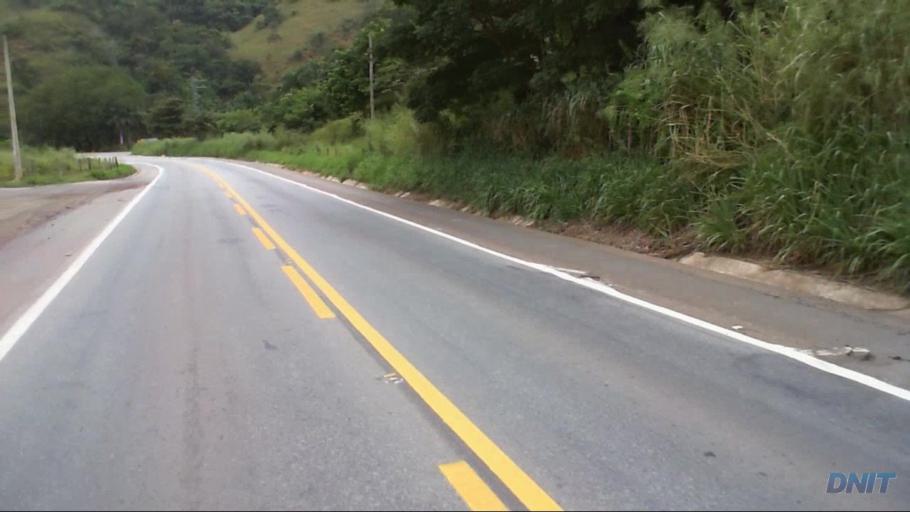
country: BR
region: Minas Gerais
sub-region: Timoteo
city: Timoteo
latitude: -19.5732
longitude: -42.7151
